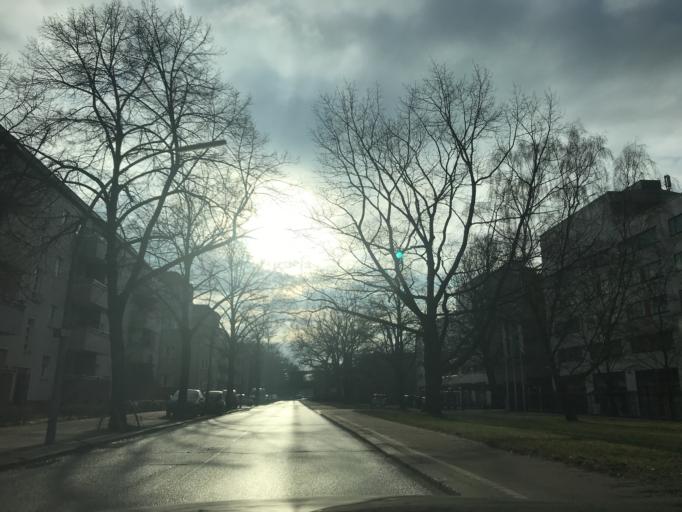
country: DE
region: Berlin
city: Siemensstadt
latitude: 52.5415
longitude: 13.2624
